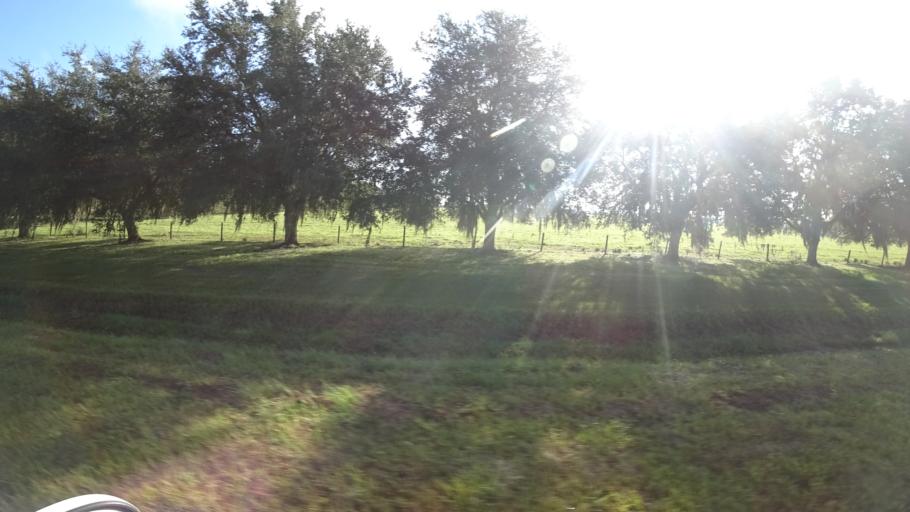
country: US
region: Florida
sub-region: Sarasota County
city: The Meadows
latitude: 27.4256
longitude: -82.3036
